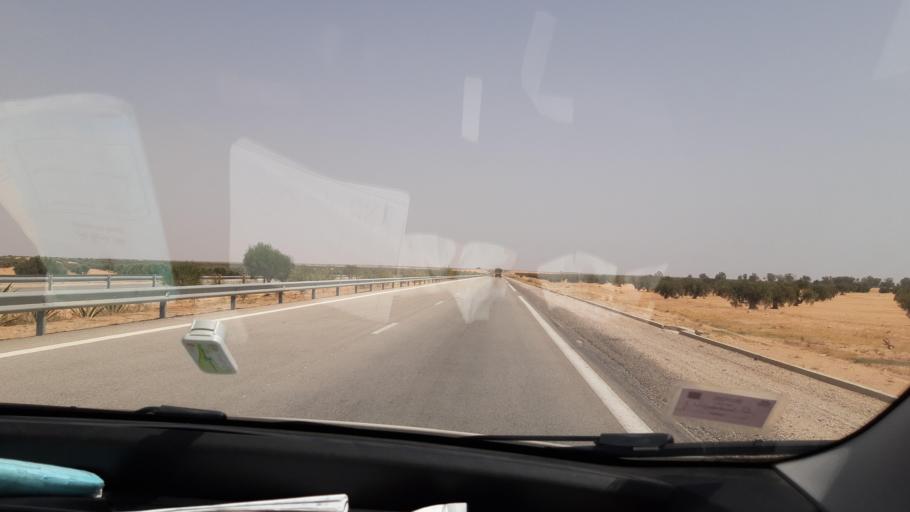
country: TN
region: Safaqis
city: Bi'r `Ali Bin Khalifah
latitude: 34.5306
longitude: 10.1042
